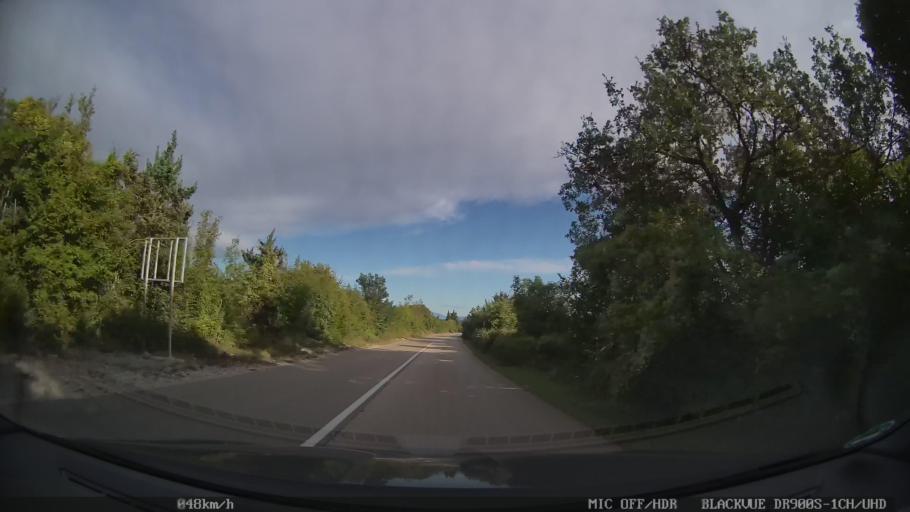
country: HR
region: Primorsko-Goranska
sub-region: Grad Krk
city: Krk
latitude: 45.0694
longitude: 14.4694
